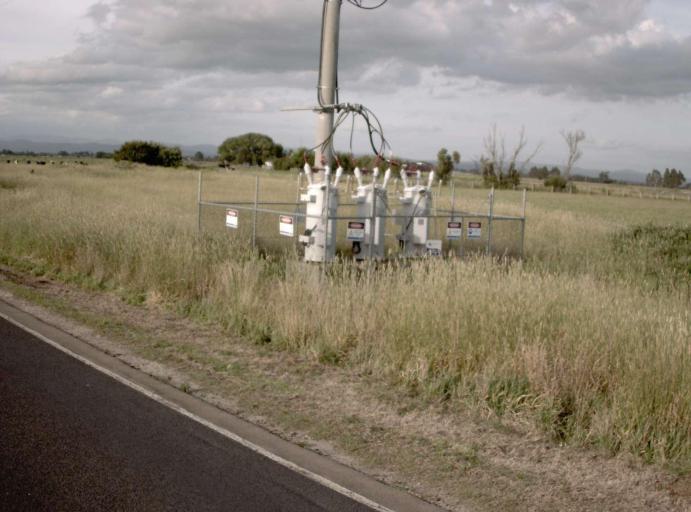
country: AU
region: Victoria
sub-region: Wellington
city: Heyfield
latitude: -37.8963
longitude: 146.9919
